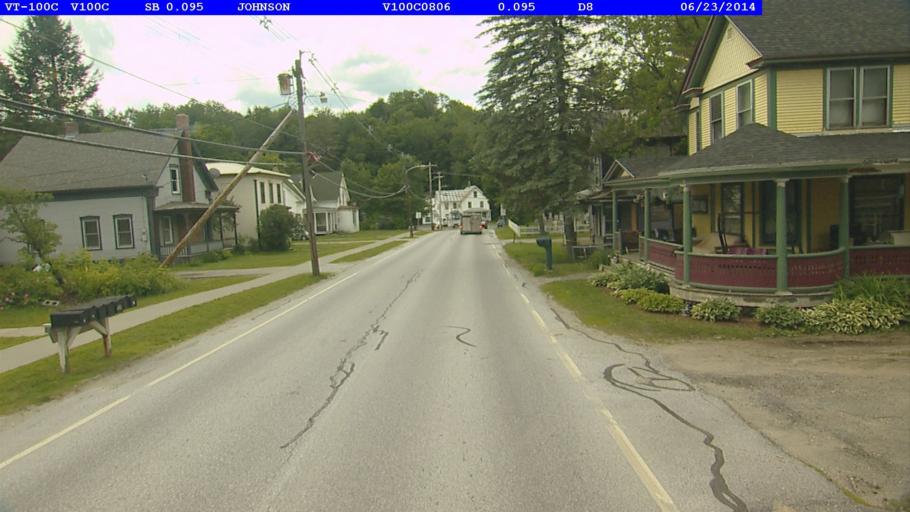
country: US
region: Vermont
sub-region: Lamoille County
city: Johnson
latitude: 44.6342
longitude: -72.6745
